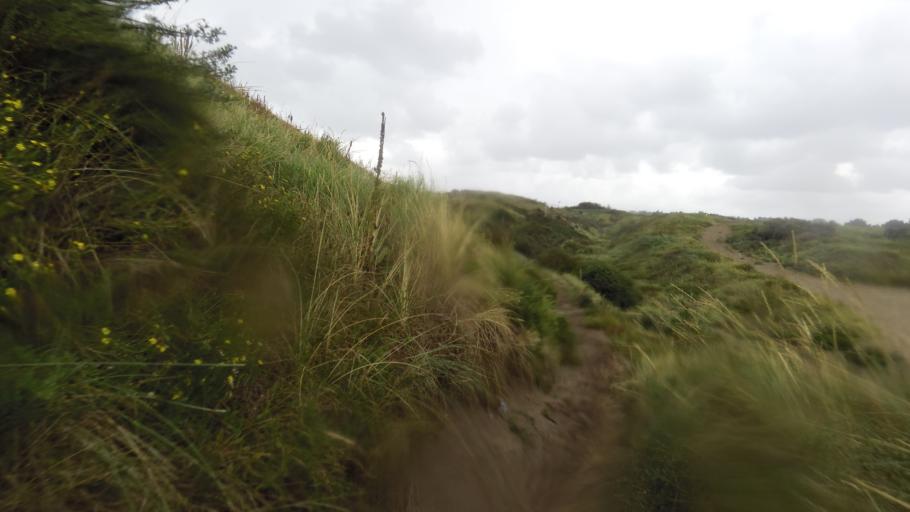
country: NL
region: North Holland
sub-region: Gemeente Zandvoort
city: Zandvoort
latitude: 52.3839
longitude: 4.5393
